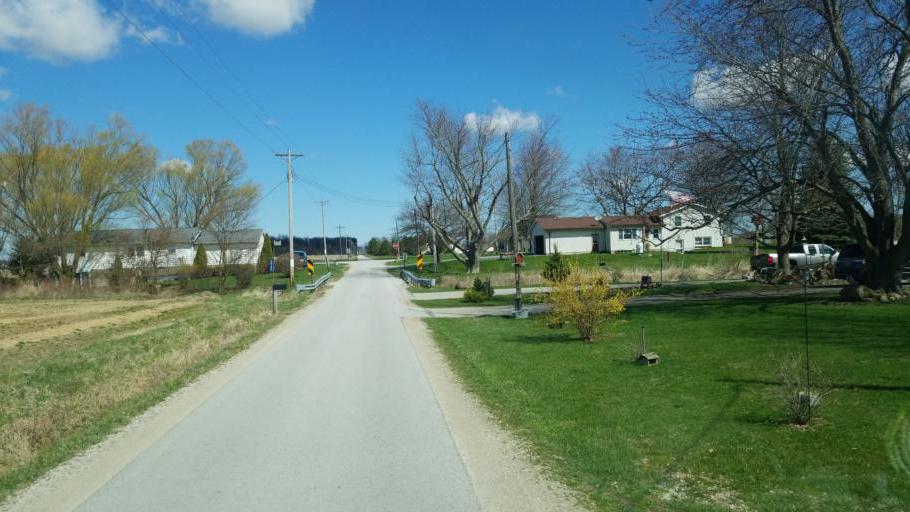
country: US
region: Ohio
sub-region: Sandusky County
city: Mount Carmel
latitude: 41.2259
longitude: -82.9371
